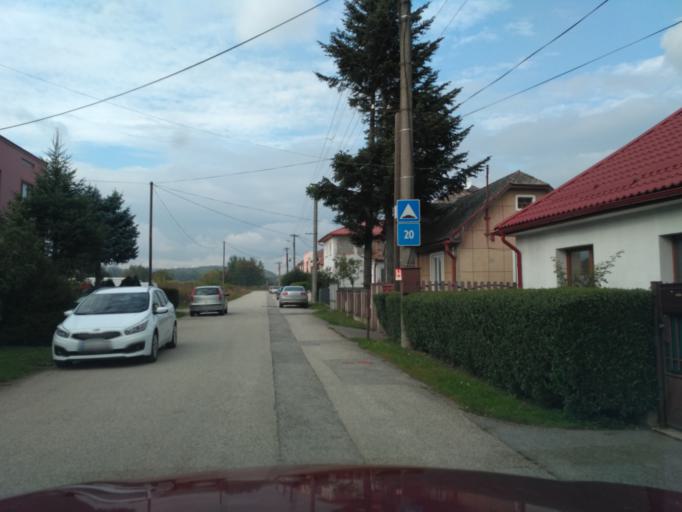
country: SK
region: Kosicky
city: Kosice
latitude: 48.6399
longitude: 21.1687
